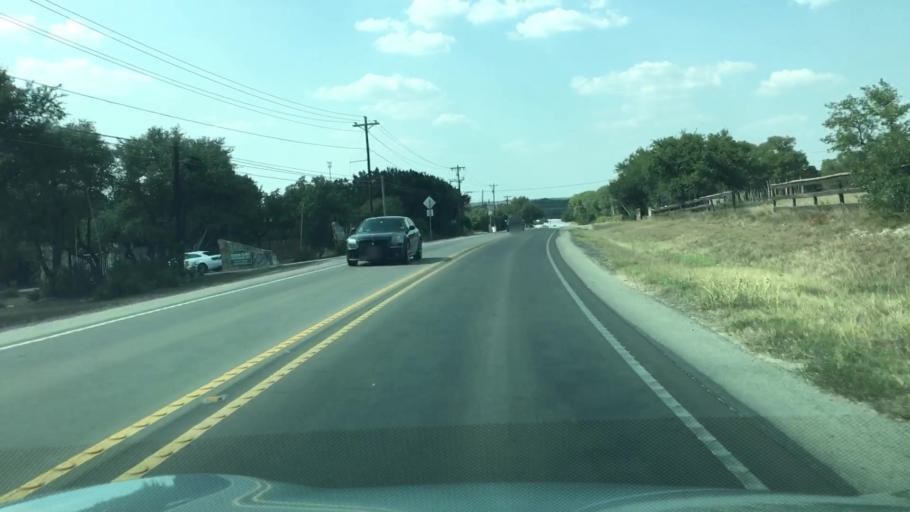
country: US
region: Texas
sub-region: Hays County
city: Woodcreek
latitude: 30.0366
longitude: -98.1022
